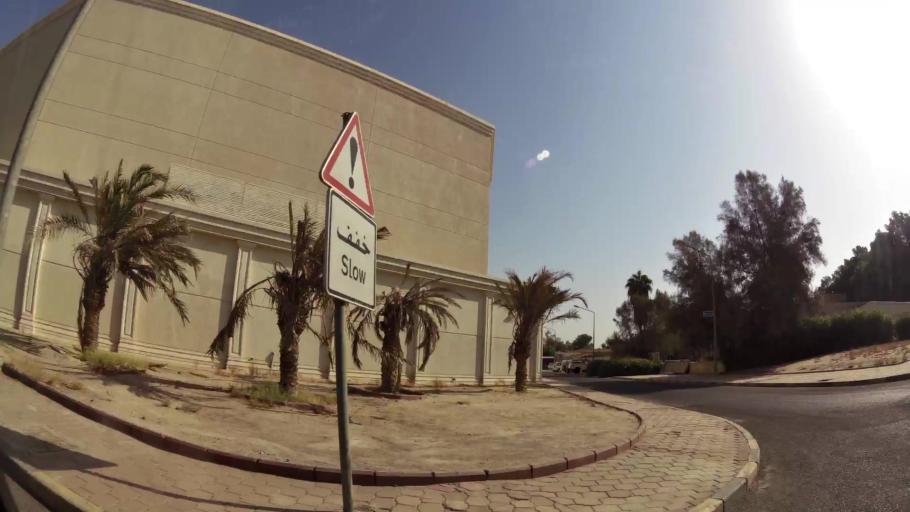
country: KW
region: Al Asimah
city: Ash Shamiyah
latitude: 29.3536
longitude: 47.9441
